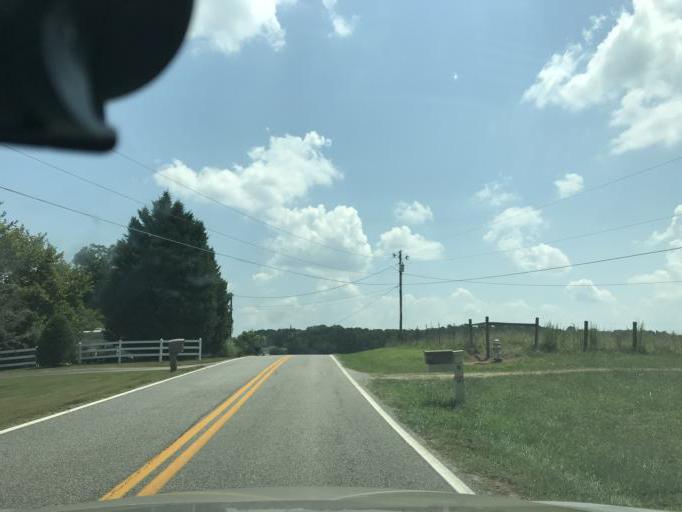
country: US
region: Georgia
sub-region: Forsyth County
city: Cumming
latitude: 34.3162
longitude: -84.1527
